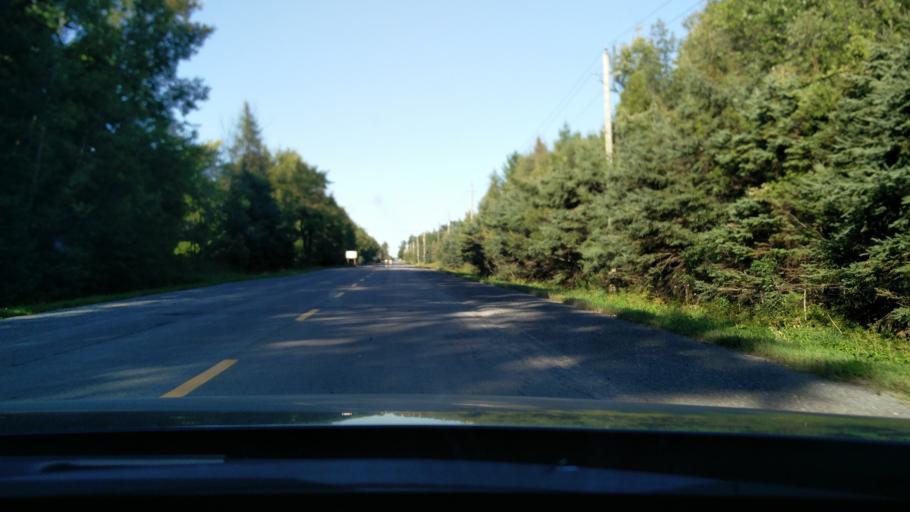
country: CA
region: Ontario
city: Bells Corners
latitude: 45.1744
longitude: -75.8698
